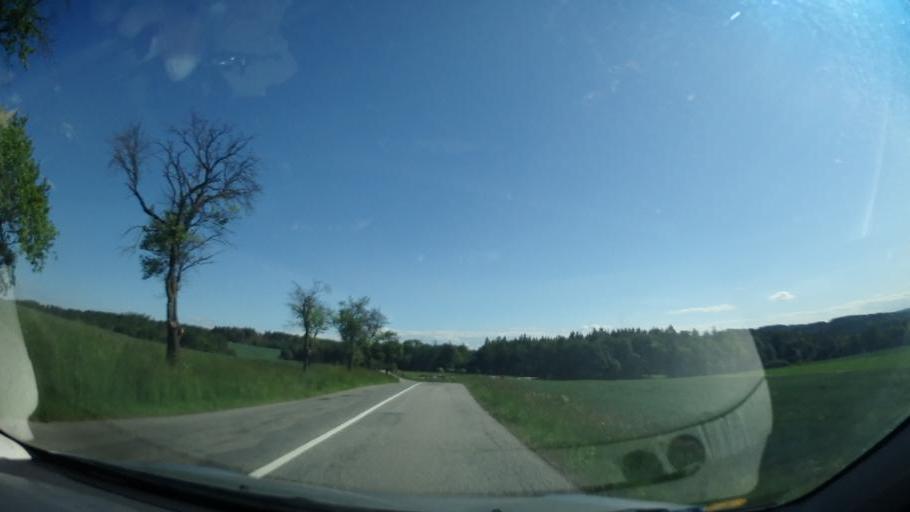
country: CZ
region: South Moravian
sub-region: Okres Blansko
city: Letovice
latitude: 49.5739
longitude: 16.5832
